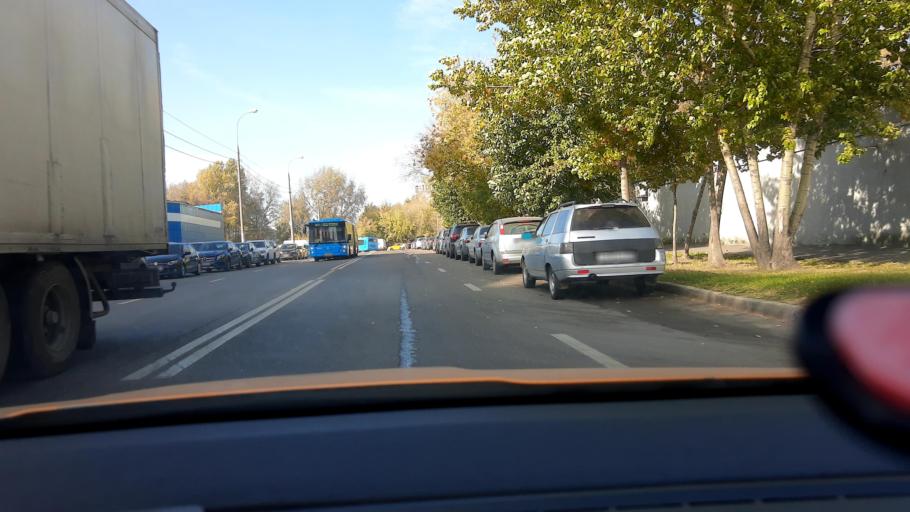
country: RU
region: Moscow
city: Nagornyy
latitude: 55.6472
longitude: 37.6327
